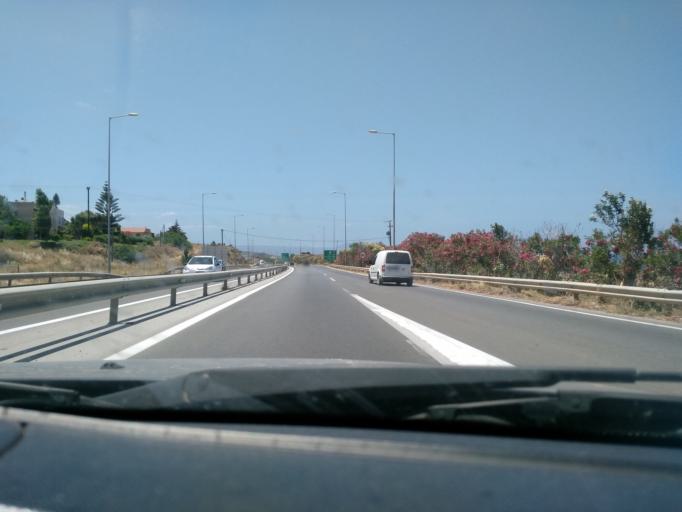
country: GR
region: Crete
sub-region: Nomos Rethymnis
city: Rethymno
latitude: 35.3569
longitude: 24.4649
